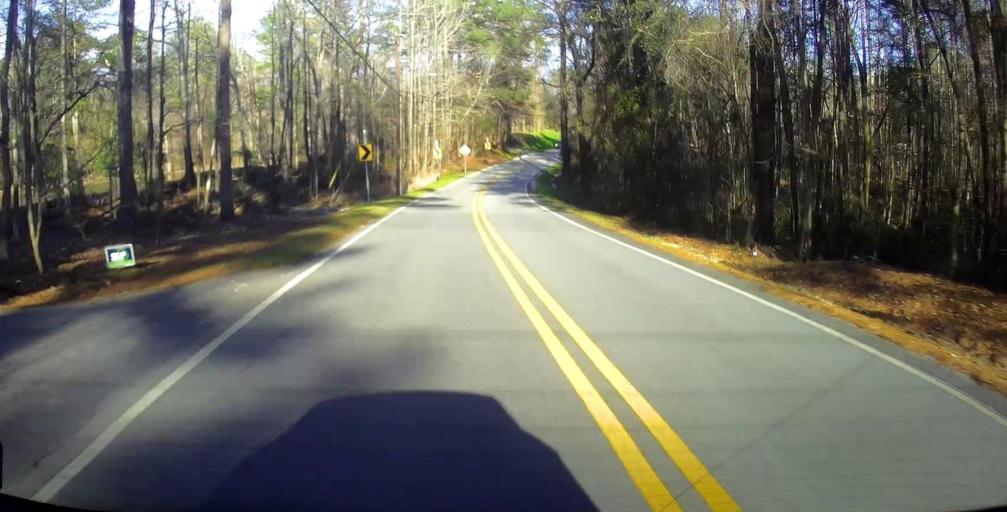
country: US
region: Georgia
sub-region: Harris County
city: Hamilton
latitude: 32.5757
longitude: -84.8167
